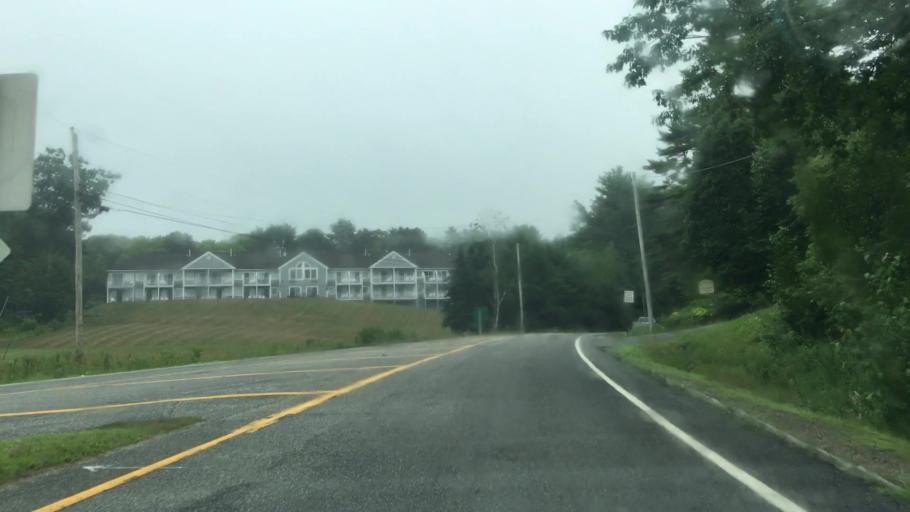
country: US
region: Maine
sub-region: Lincoln County
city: Wiscasset
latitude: 44.0012
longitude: -69.6343
